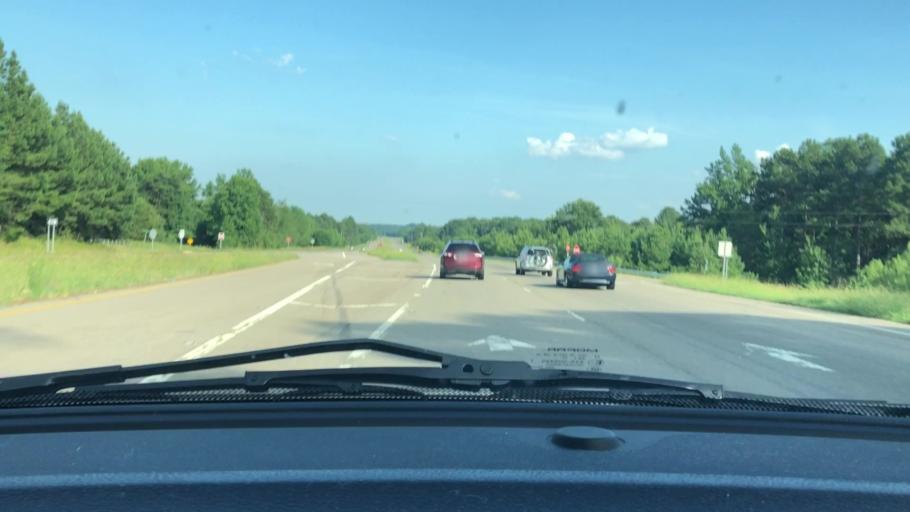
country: US
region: North Carolina
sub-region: Chatham County
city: Siler City
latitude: 35.6265
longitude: -79.3638
